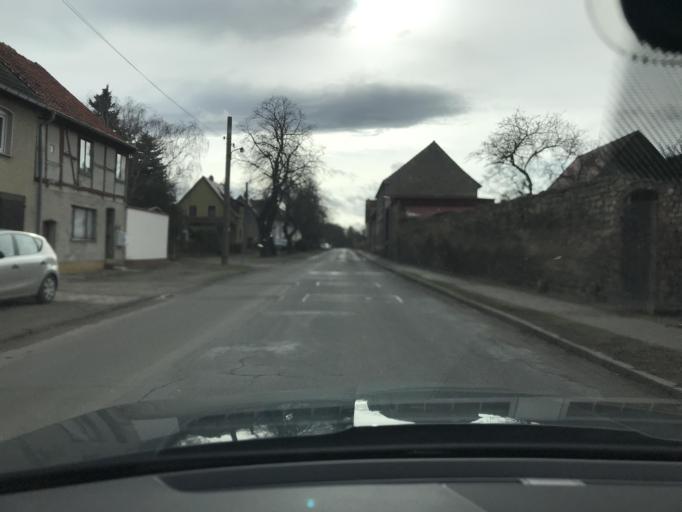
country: DE
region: Saxony-Anhalt
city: Wegeleben
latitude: 51.8852
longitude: 11.1770
